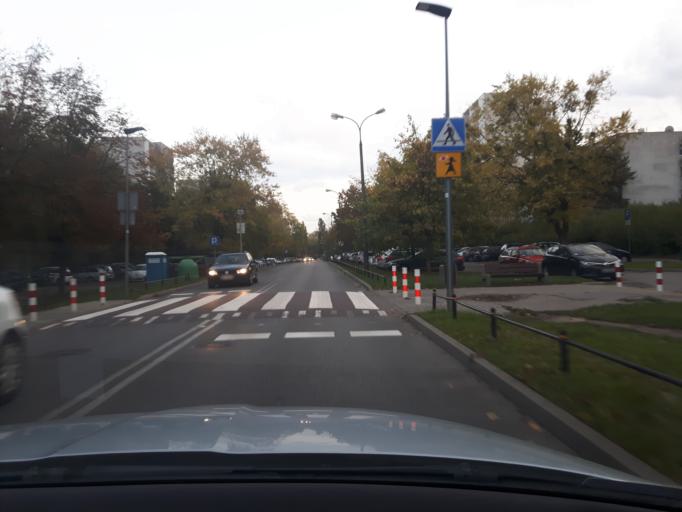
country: PL
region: Masovian Voivodeship
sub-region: Warszawa
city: Ursynow
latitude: 52.1397
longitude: 21.0522
